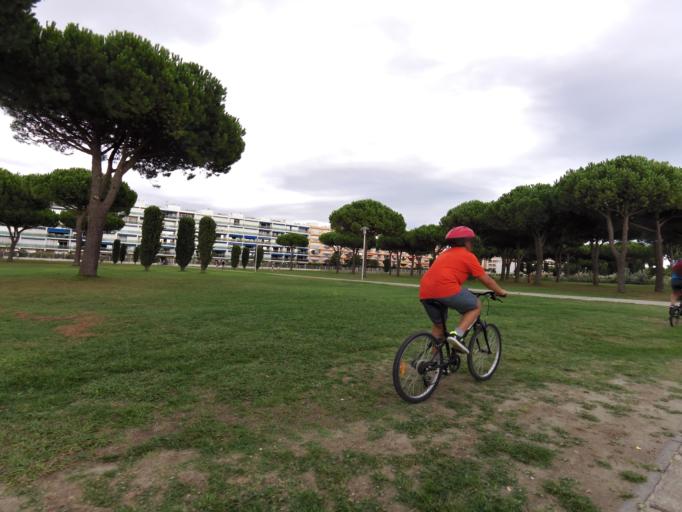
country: FR
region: Languedoc-Roussillon
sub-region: Departement du Gard
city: Le Grau-du-Roi
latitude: 43.5297
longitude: 4.1400
